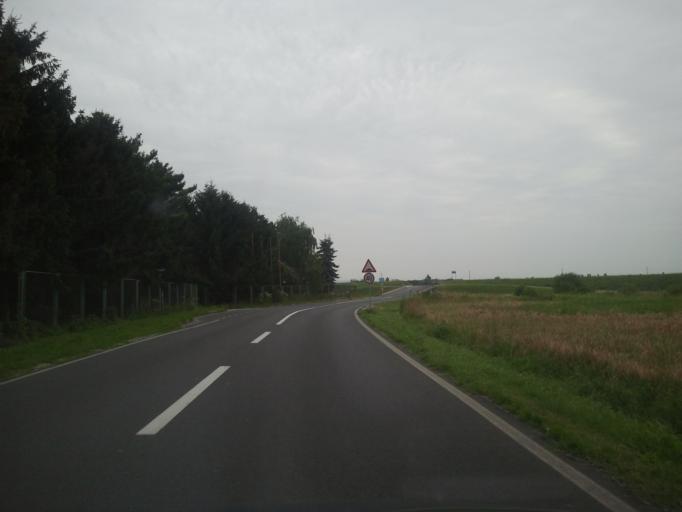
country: HR
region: Grad Zagreb
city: Zadvorsko
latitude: 45.7451
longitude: 15.9186
